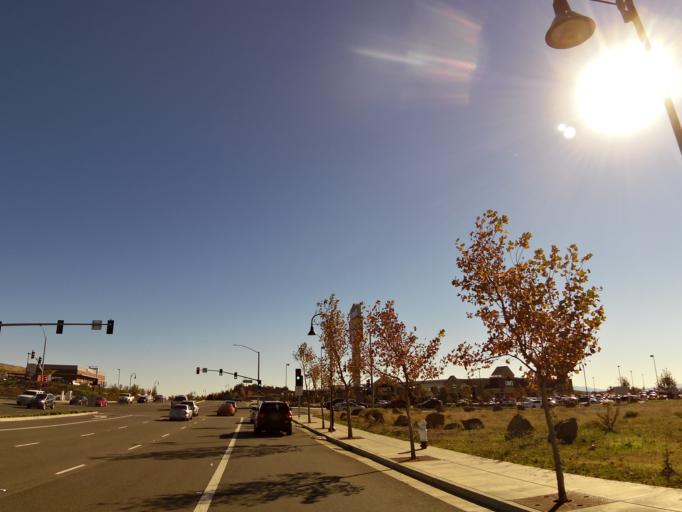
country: US
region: California
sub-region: Solano County
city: Fairfield
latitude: 38.2941
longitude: -122.0325
